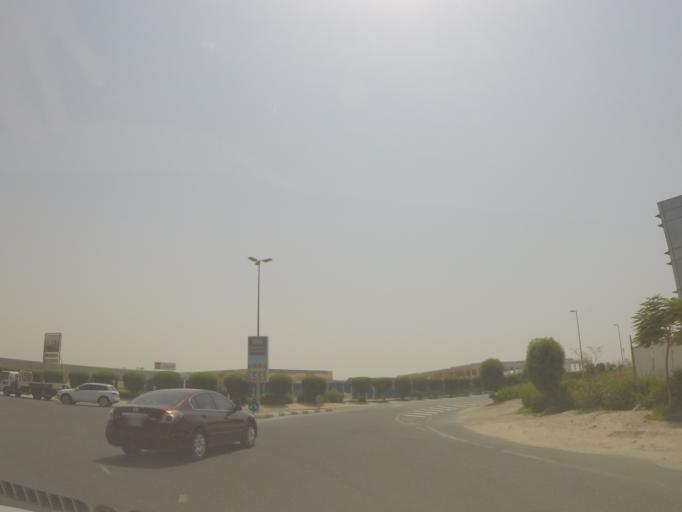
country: AE
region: Dubai
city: Dubai
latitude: 25.0028
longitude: 55.1547
